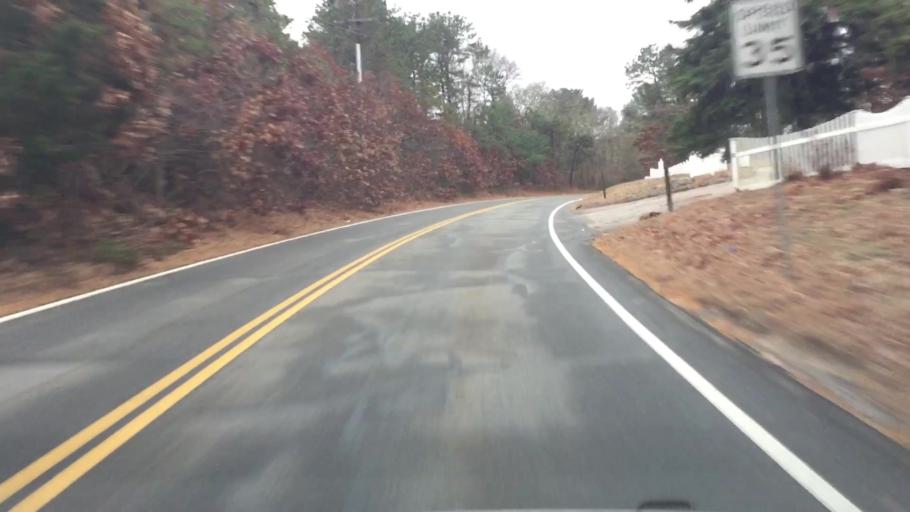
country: US
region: Massachusetts
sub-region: Barnstable County
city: West Falmouth
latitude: 41.6204
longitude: -70.6372
